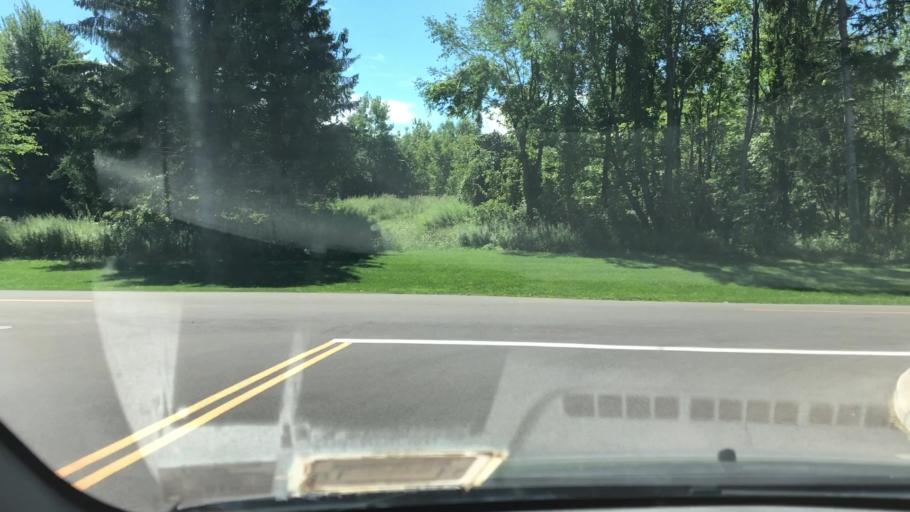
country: US
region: New York
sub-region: Monroe County
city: Webster
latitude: 43.2080
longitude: -77.4587
